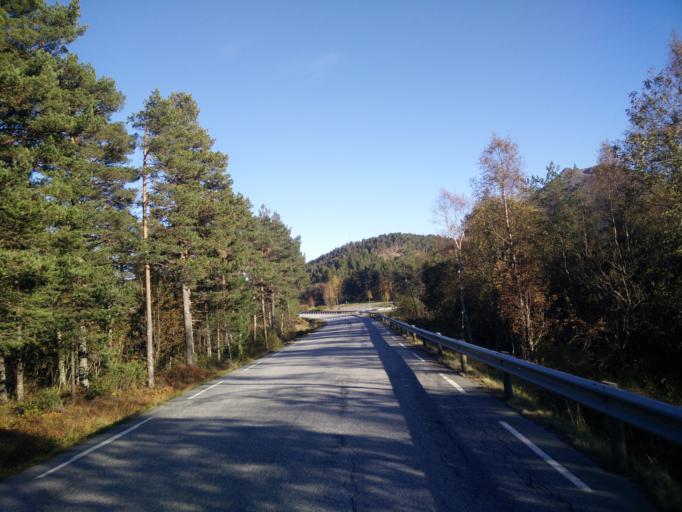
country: NO
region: More og Romsdal
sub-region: Halsa
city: Liaboen
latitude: 63.1265
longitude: 8.3703
